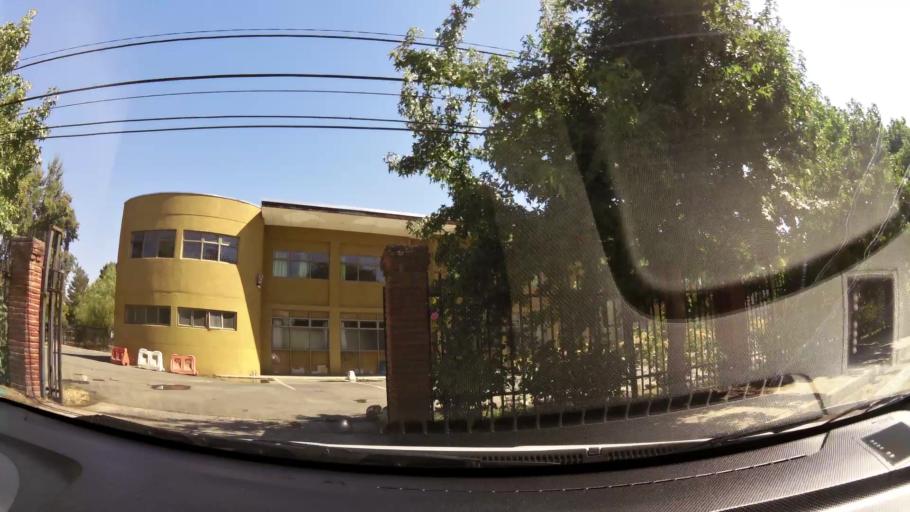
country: CL
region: Maule
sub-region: Provincia de Talca
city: Talca
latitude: -35.4348
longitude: -71.6044
